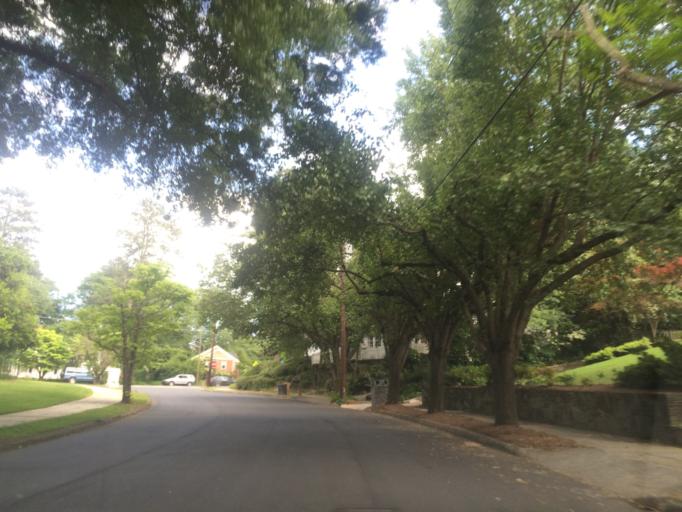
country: US
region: Georgia
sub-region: DeKalb County
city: Druid Hills
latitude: 33.7987
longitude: -84.3506
